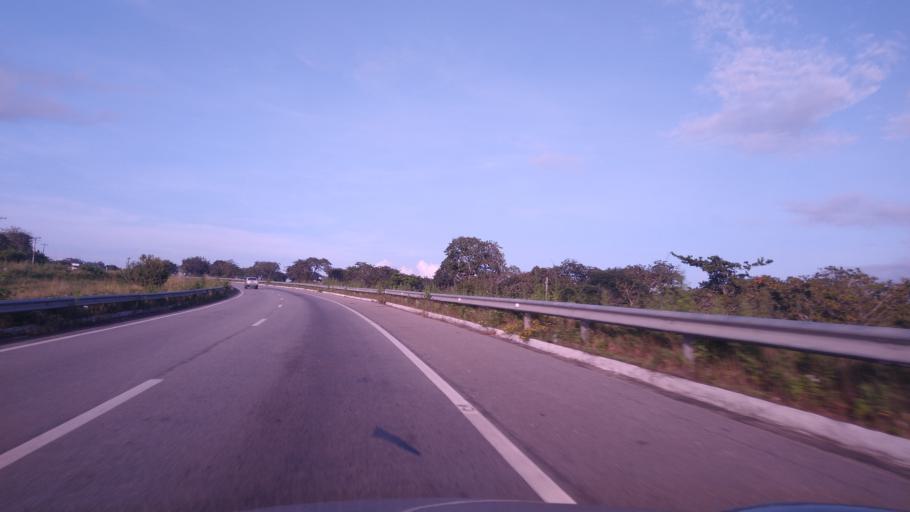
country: BR
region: Ceara
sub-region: Pacajus
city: Pacajus
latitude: -4.1670
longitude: -38.4919
